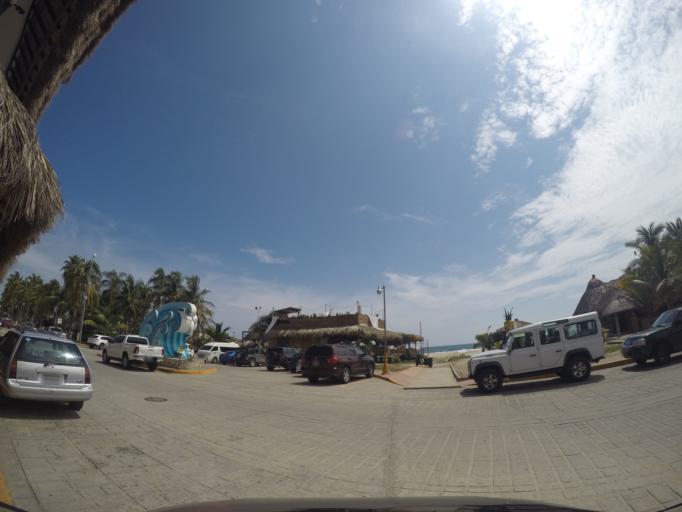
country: MX
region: Oaxaca
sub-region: Santa Maria Colotepec
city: Brisas de Zicatela
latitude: 15.8544
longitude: -97.0562
